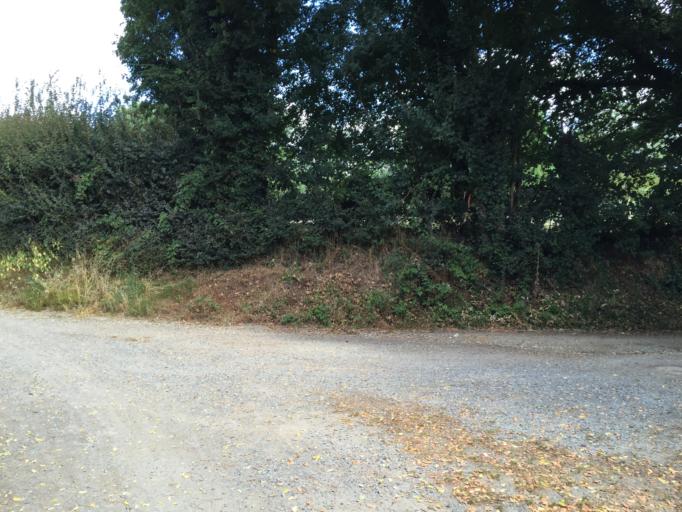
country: FR
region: Pays de la Loire
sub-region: Departement de la Sarthe
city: Allonnes
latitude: 47.9592
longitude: 0.1707
